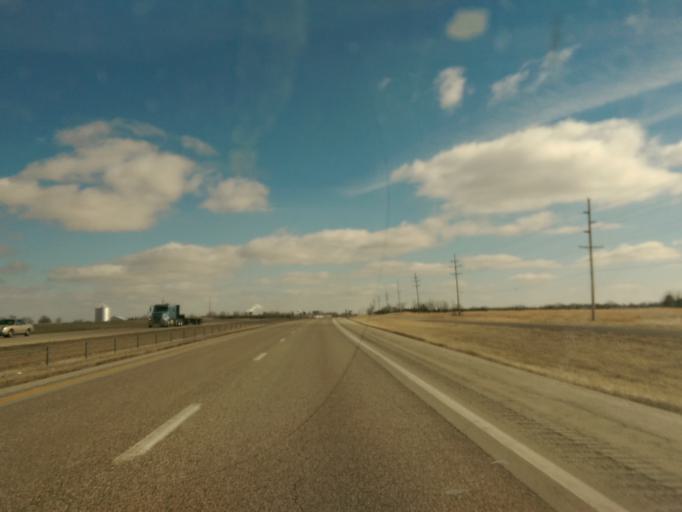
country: US
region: Missouri
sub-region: Montgomery County
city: Montgomery City
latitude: 38.8850
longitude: -91.4053
